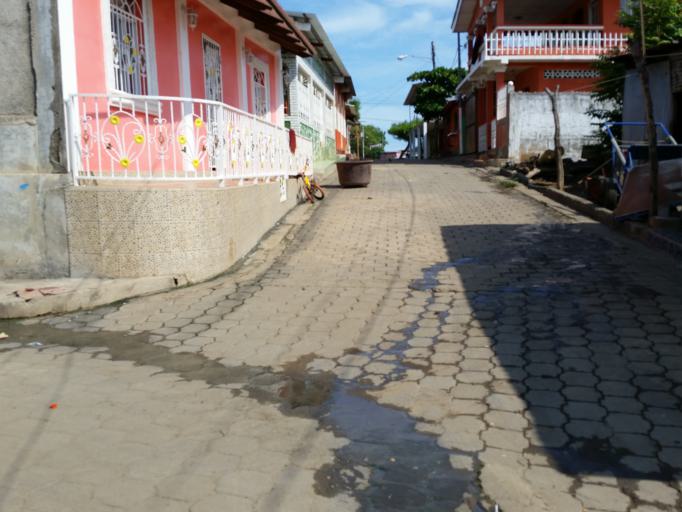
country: NI
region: Managua
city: Masachapa
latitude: 11.7863
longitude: -86.5152
